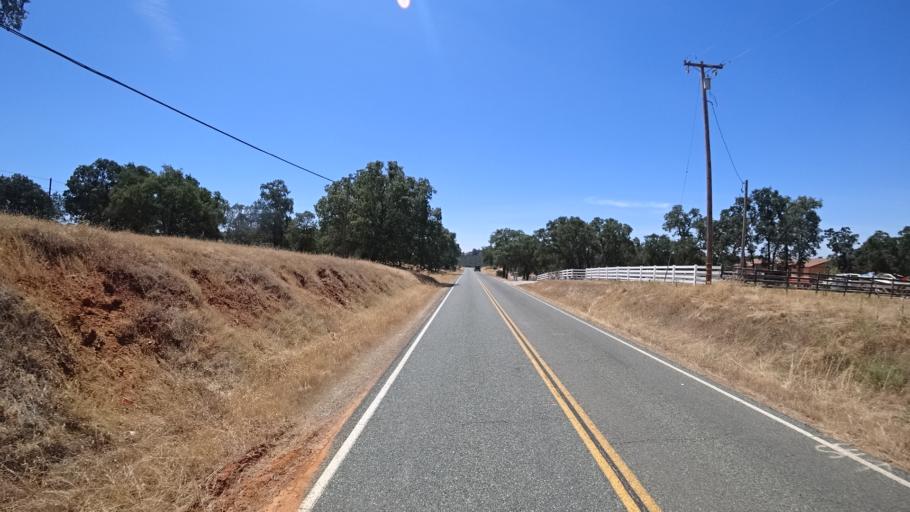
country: US
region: California
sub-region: Calaveras County
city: Valley Springs
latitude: 38.2044
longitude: -120.9051
